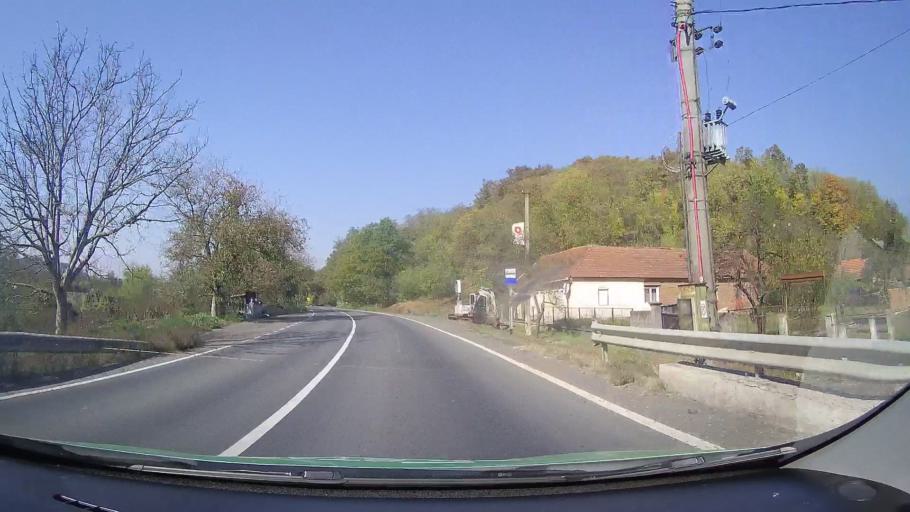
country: RO
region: Arad
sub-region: Comuna Savarsin
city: Savarsin
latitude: 45.9980
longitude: 22.2906
